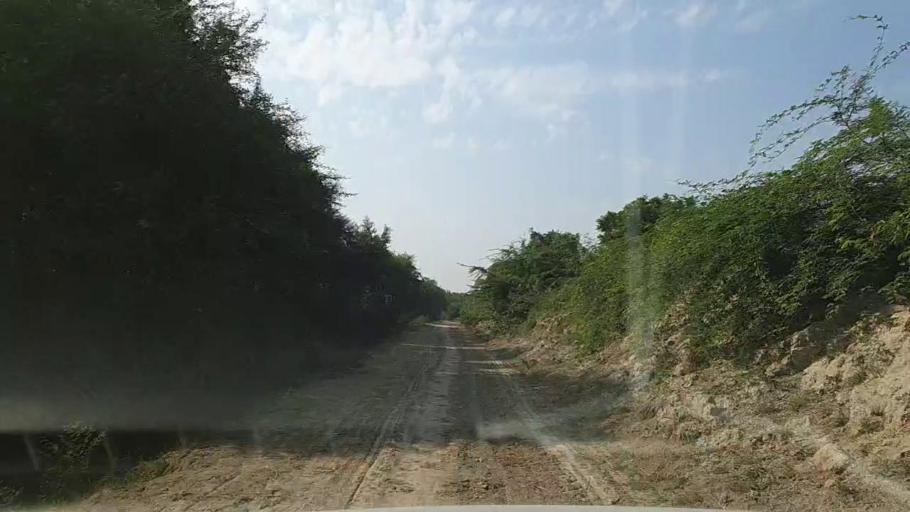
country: PK
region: Sindh
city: Mirpur Batoro
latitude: 24.7066
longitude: 68.3033
